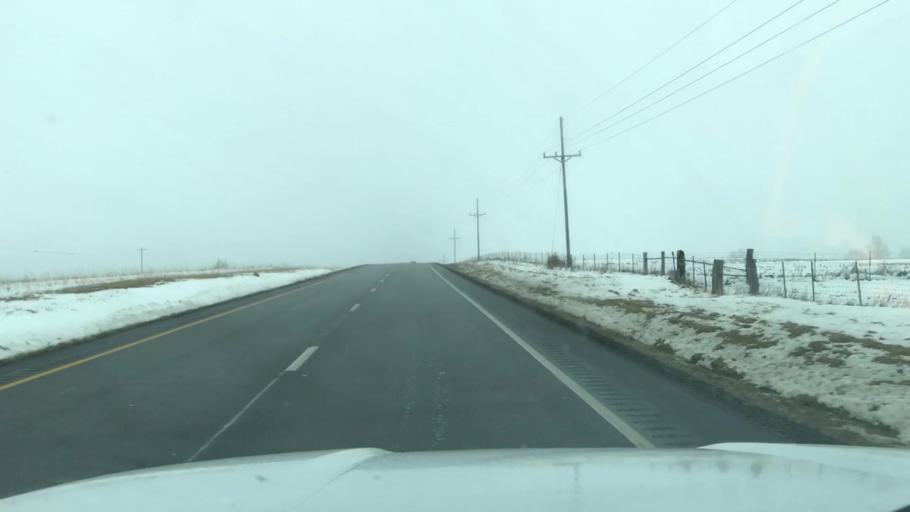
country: US
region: Missouri
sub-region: Clinton County
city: Cameron
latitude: 39.7541
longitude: -94.2774
